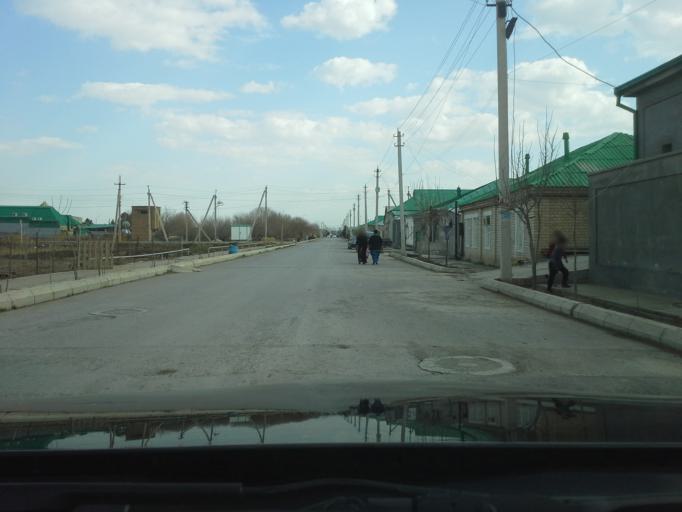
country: TM
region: Ahal
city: Ashgabat
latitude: 37.9915
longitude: 58.2848
